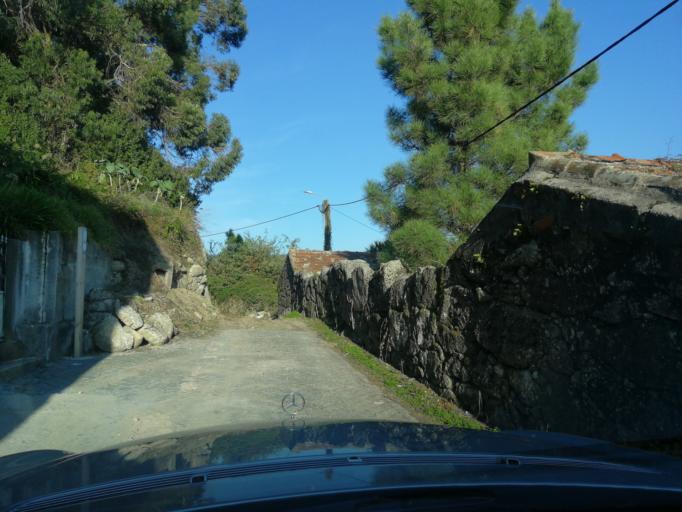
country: PT
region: Braga
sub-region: Braga
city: Oliveira
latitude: 41.4547
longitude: -8.4604
